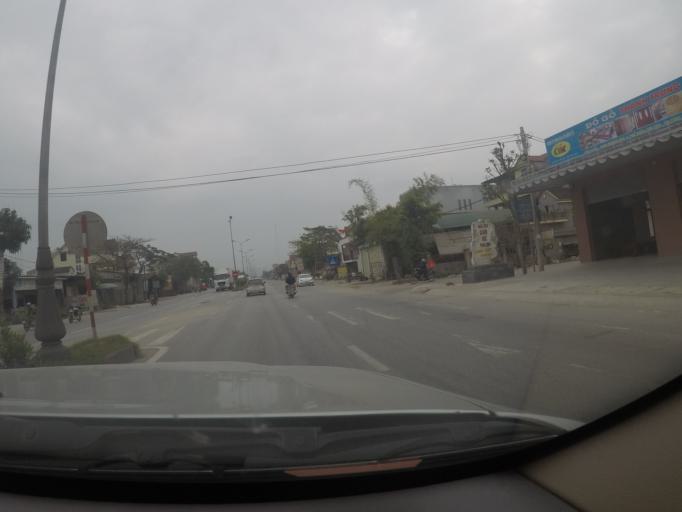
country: VN
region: Nghe An
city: Dien Chau
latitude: 18.9598
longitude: 105.6017
